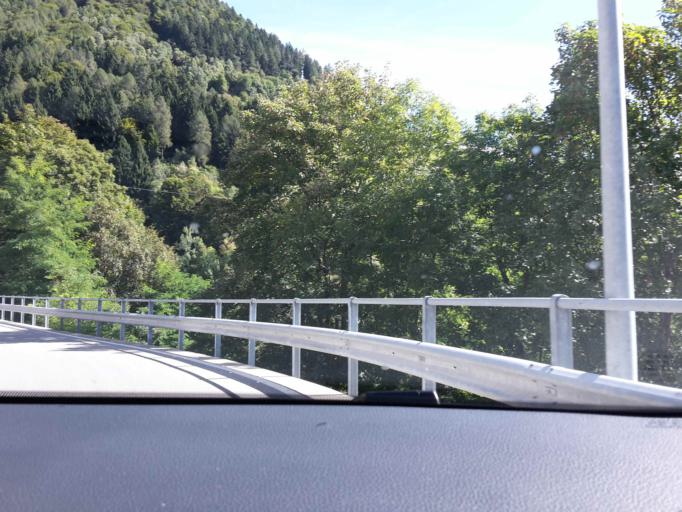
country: CH
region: Ticino
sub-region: Bellinzona District
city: Lumino
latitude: 46.1701
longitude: 9.0810
